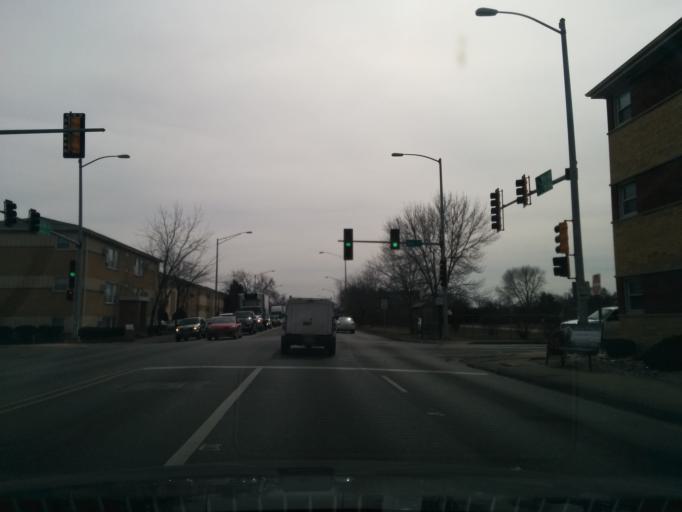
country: US
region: Illinois
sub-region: Cook County
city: Berwyn
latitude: 41.8580
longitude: -87.8040
